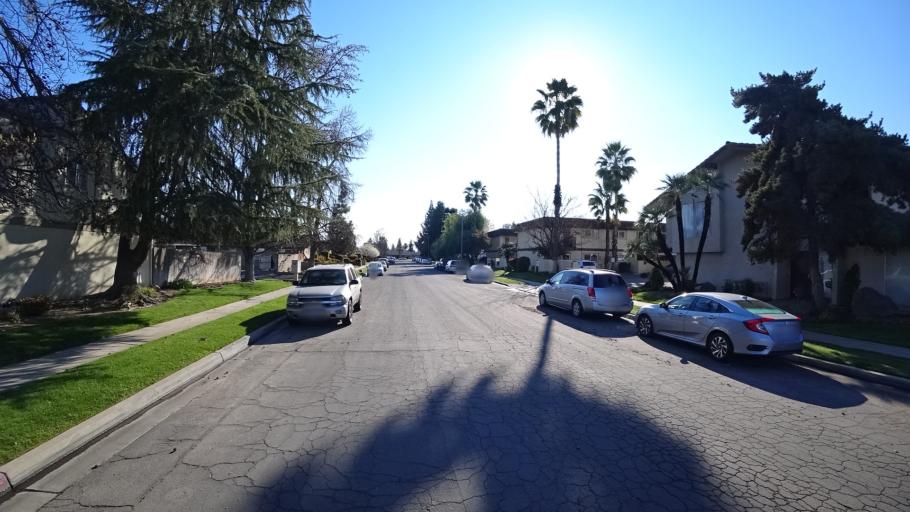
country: US
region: California
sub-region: Fresno County
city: Fresno
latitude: 36.8244
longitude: -119.7811
